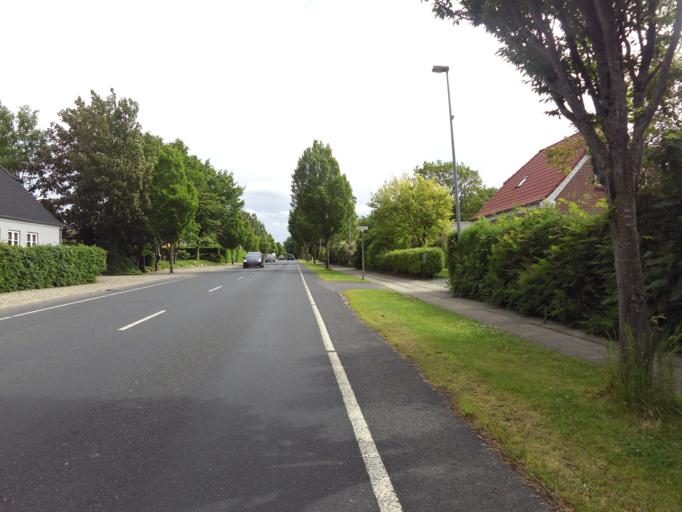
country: DK
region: South Denmark
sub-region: Vejen Kommune
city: Rodding
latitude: 55.3607
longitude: 9.0577
